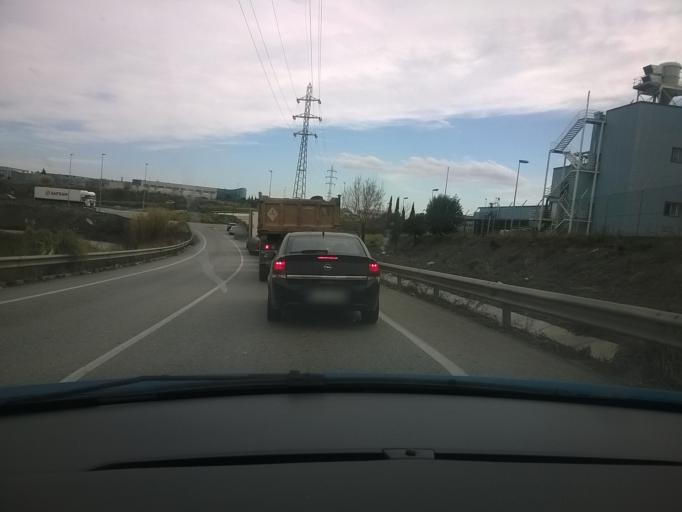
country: ES
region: Catalonia
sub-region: Provincia de Barcelona
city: Ripollet
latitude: 41.5213
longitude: 2.1522
